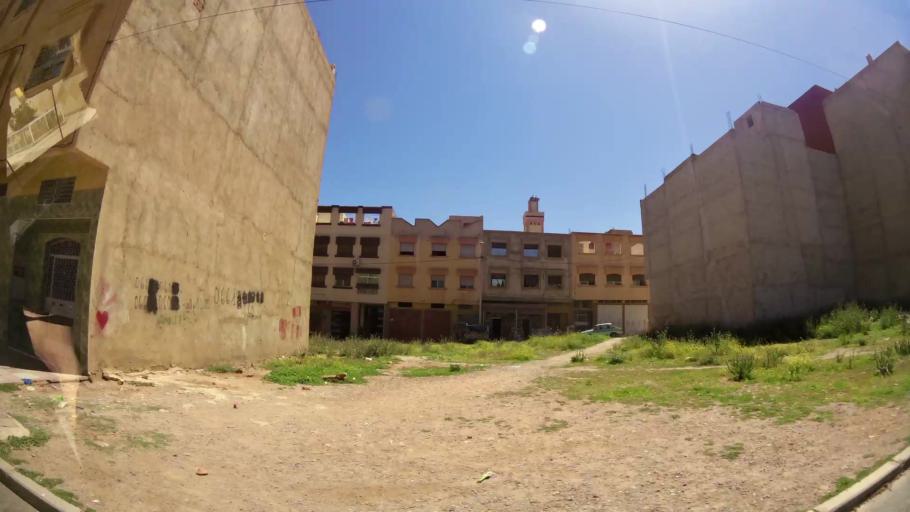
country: MA
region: Oriental
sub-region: Oujda-Angad
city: Oujda
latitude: 34.6602
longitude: -1.8781
